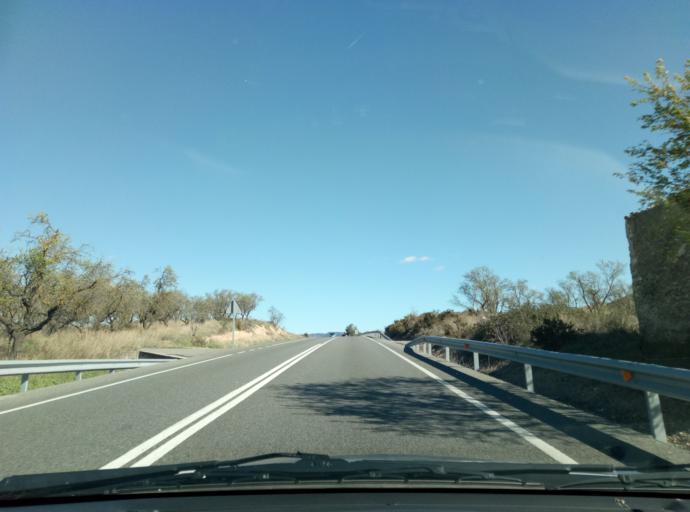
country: ES
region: Catalonia
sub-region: Provincia de Tarragona
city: Montblanc
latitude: 41.4000
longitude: 1.1093
